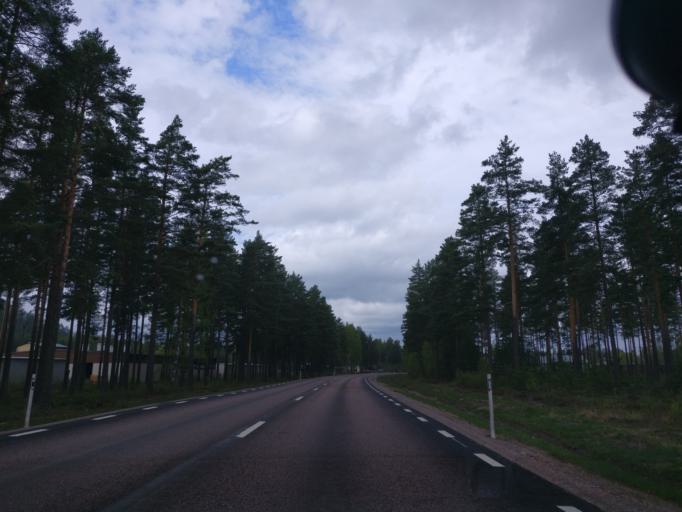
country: SE
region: Vaermland
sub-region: Hagfors Kommun
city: Ekshaerad
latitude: 60.1642
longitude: 13.5006
